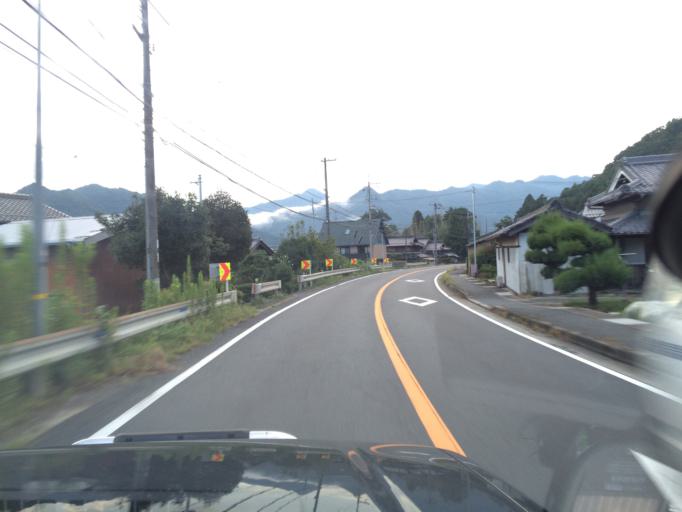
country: JP
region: Hyogo
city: Nishiwaki
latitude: 35.0924
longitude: 134.9985
